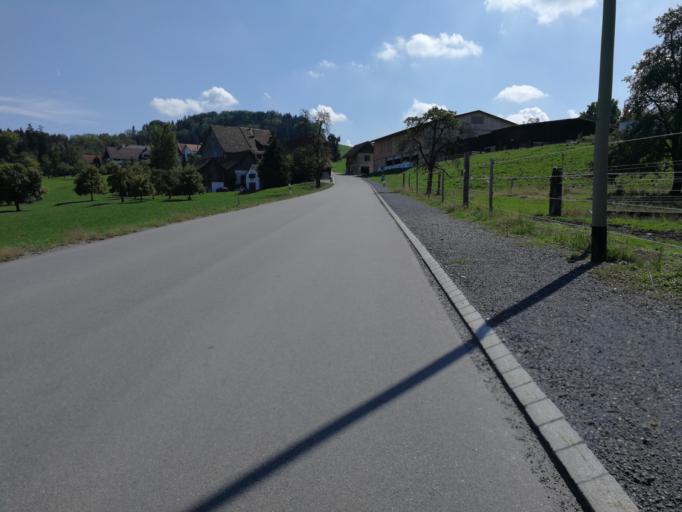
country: CH
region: Zurich
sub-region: Bezirk Horgen
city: Au / Unter-Dorf
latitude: 47.2417
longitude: 8.6249
